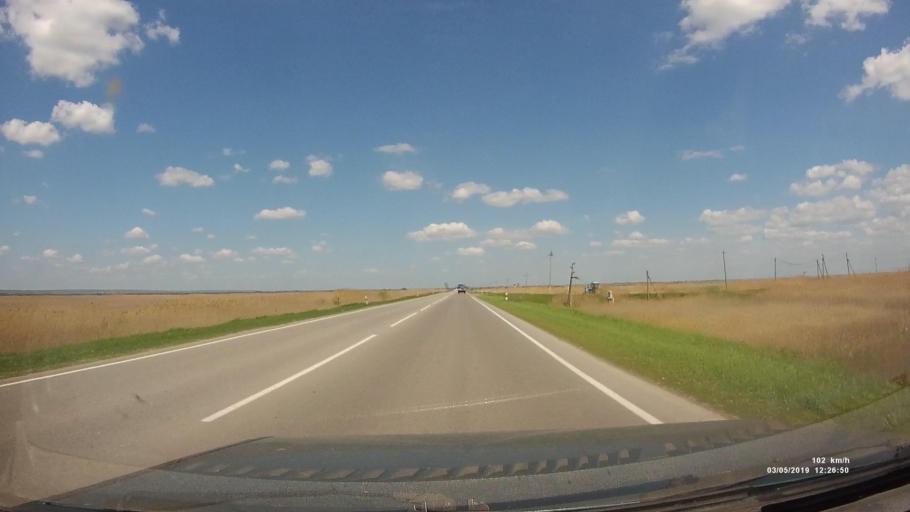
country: RU
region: Rostov
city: Semikarakorsk
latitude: 47.4511
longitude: 40.7168
